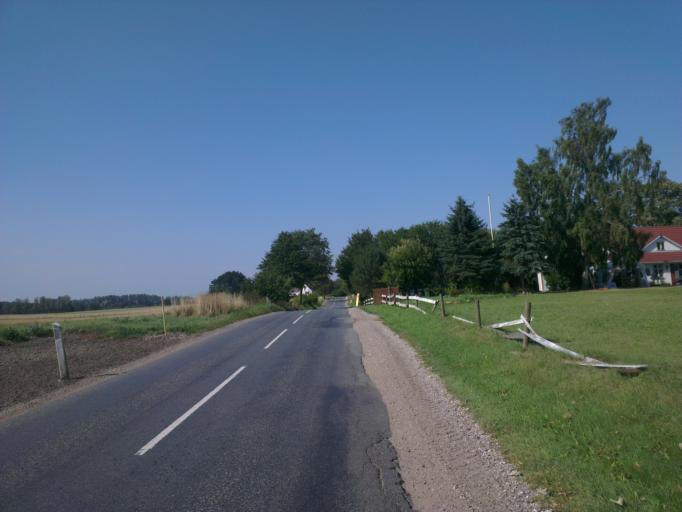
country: DK
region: Capital Region
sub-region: Frederikssund Kommune
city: Skibby
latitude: 55.7694
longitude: 11.9462
